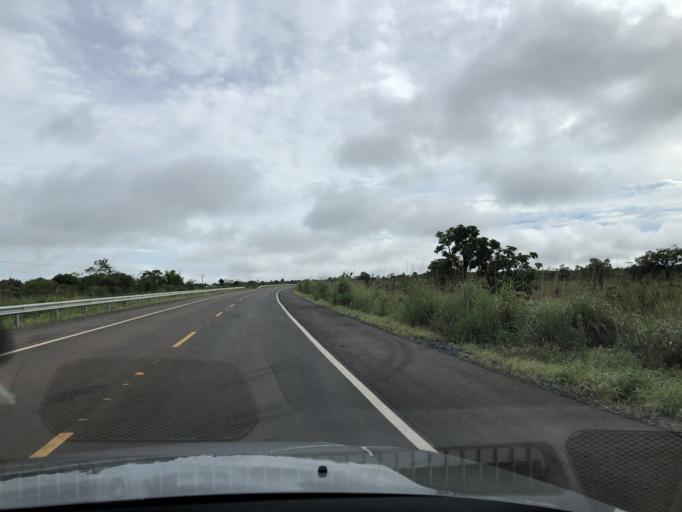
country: BR
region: Federal District
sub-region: Brasilia
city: Brasilia
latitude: -15.6309
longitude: -48.0760
